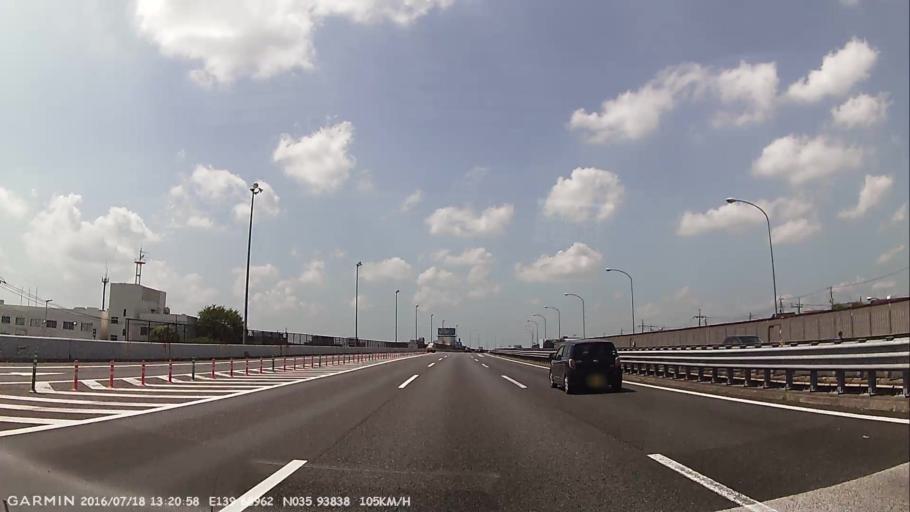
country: JP
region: Saitama
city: Iwatsuki
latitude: 35.9386
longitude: 139.6894
